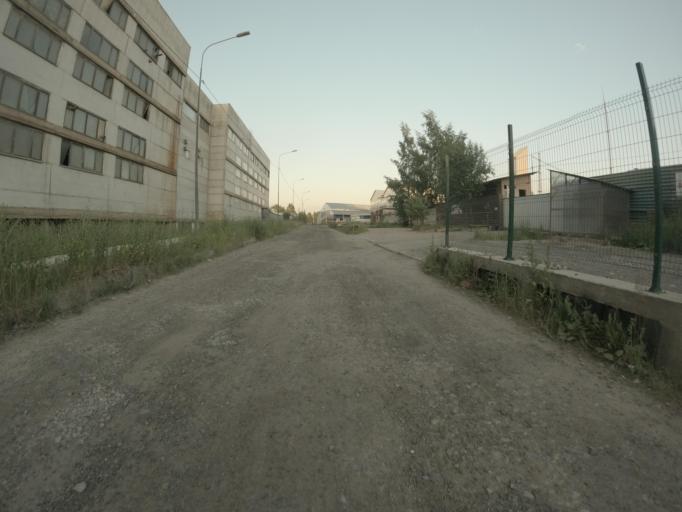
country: RU
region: St.-Petersburg
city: Admiralteisky
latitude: 59.8860
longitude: 30.2904
